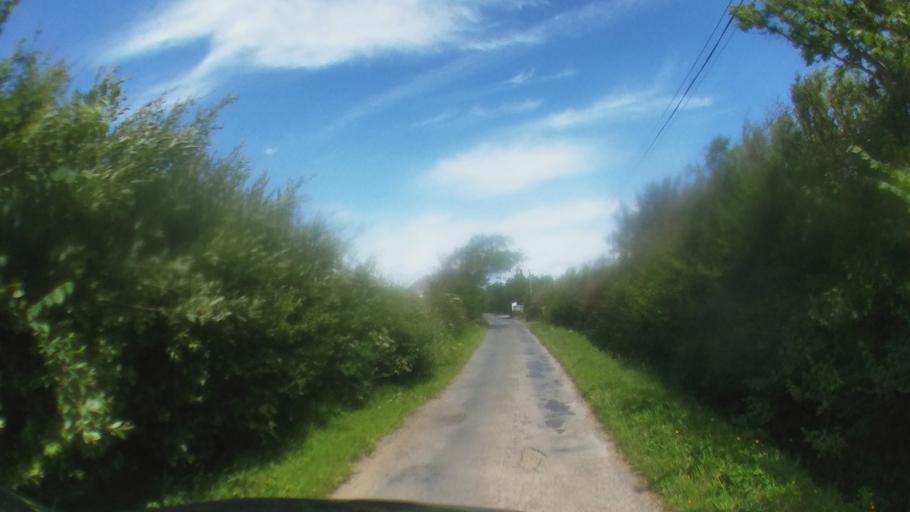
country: IE
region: Leinster
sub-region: Loch Garman
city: Loch Garman
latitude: 52.1880
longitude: -6.5422
